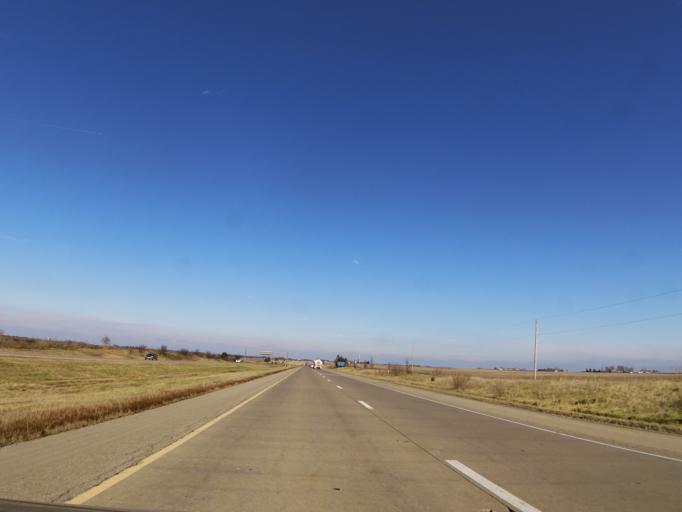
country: US
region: Illinois
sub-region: LaSalle County
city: La Salle
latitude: 41.3857
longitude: -89.0577
